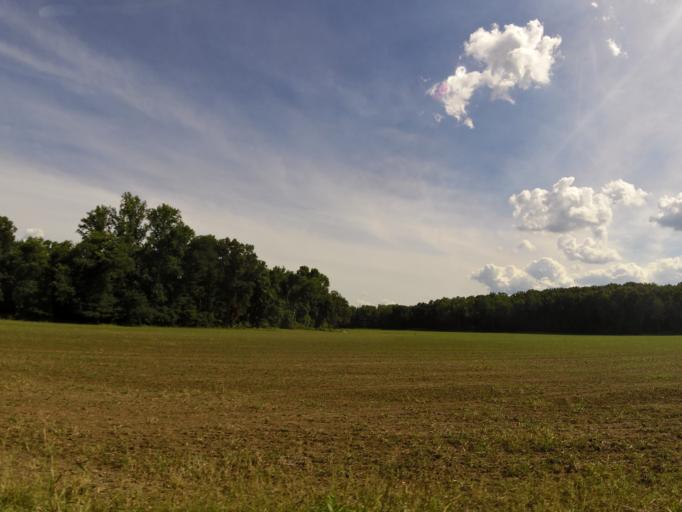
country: US
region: Tennessee
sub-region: Carroll County
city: Huntingdon
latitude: 36.0138
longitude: -88.4817
